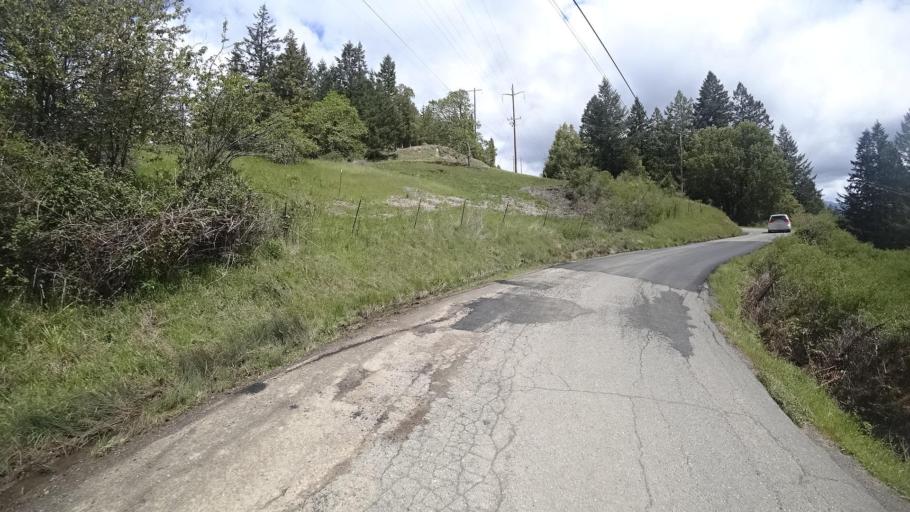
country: US
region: California
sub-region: Humboldt County
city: Blue Lake
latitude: 40.7665
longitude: -123.9399
